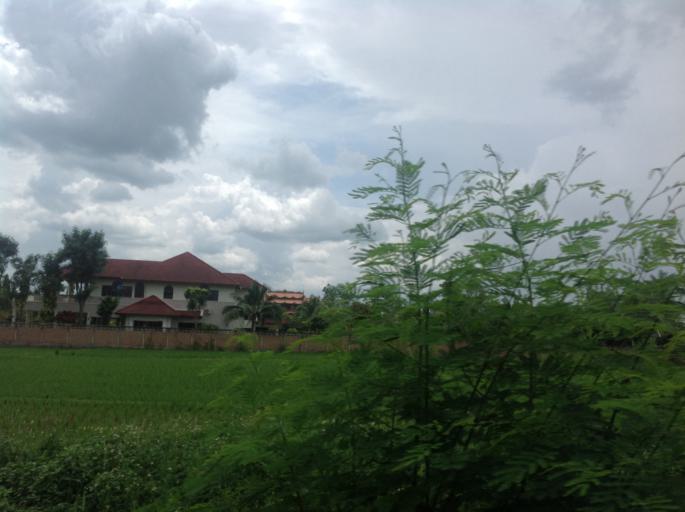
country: TH
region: Chiang Mai
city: Hang Dong
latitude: 18.6733
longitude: 98.9134
